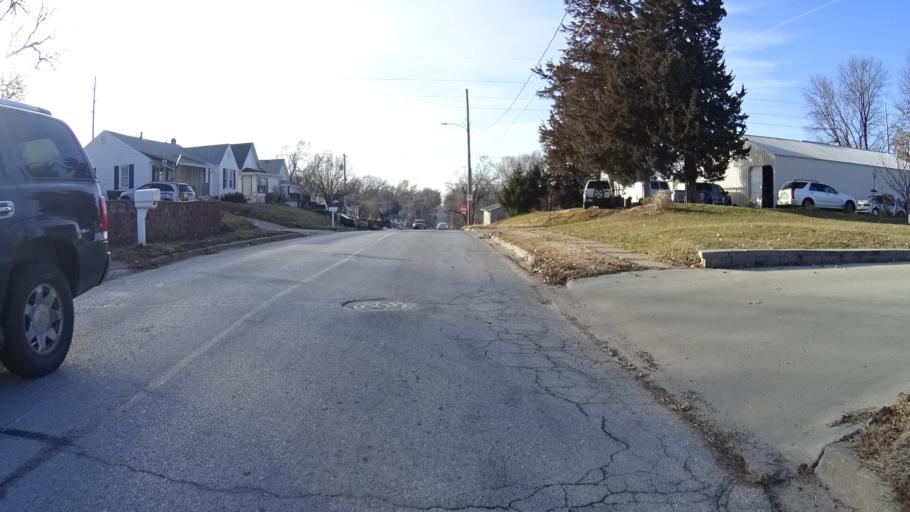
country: US
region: Nebraska
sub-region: Douglas County
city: Omaha
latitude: 41.1909
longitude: -95.9567
